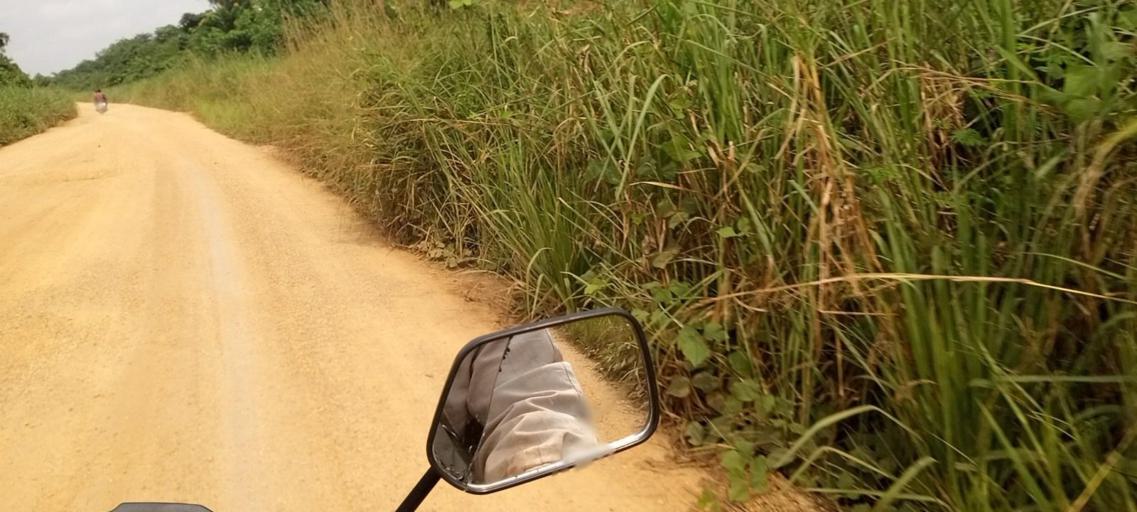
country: CD
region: Eastern Province
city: Kisangani
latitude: 0.3151
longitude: 25.4441
